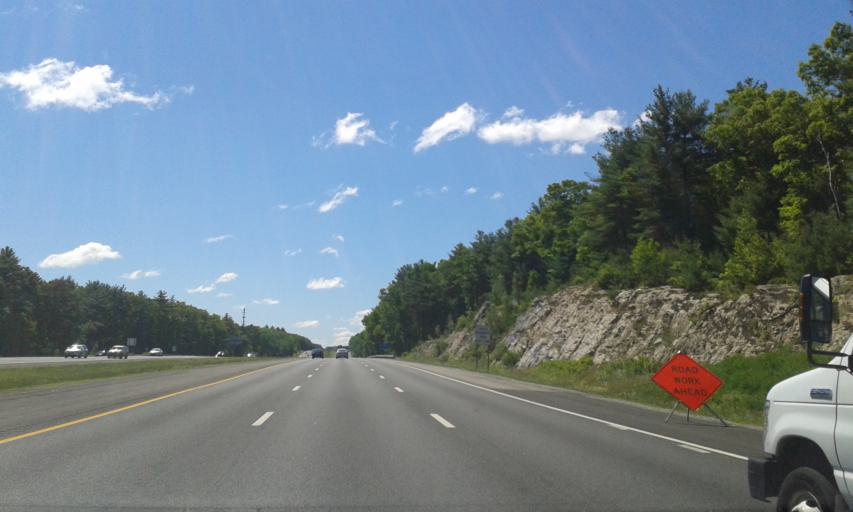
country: US
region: Massachusetts
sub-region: Middlesex County
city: Pinehurst
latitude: 42.5004
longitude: -71.2419
